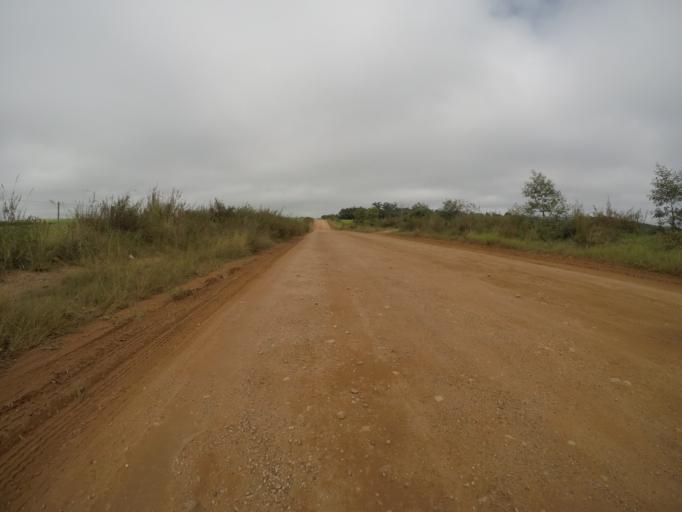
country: ZA
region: Eastern Cape
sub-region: Cacadu District Municipality
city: Kareedouw
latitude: -34.0119
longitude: 24.2372
